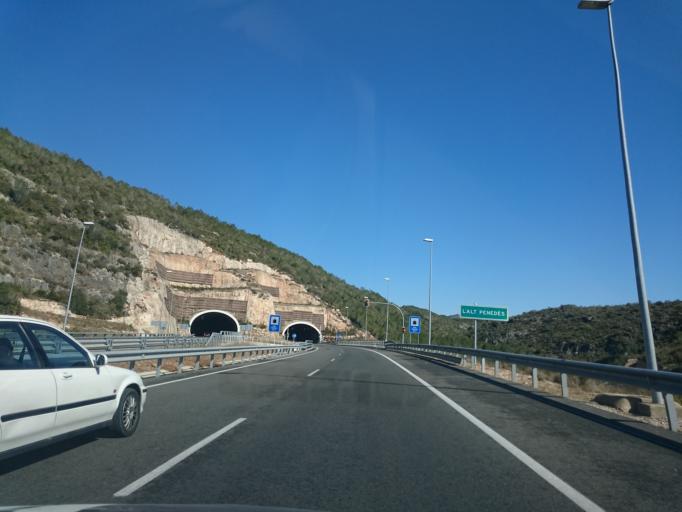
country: ES
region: Catalonia
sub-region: Provincia de Barcelona
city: Sant Pere de Ribes
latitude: 41.2971
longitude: 1.7268
